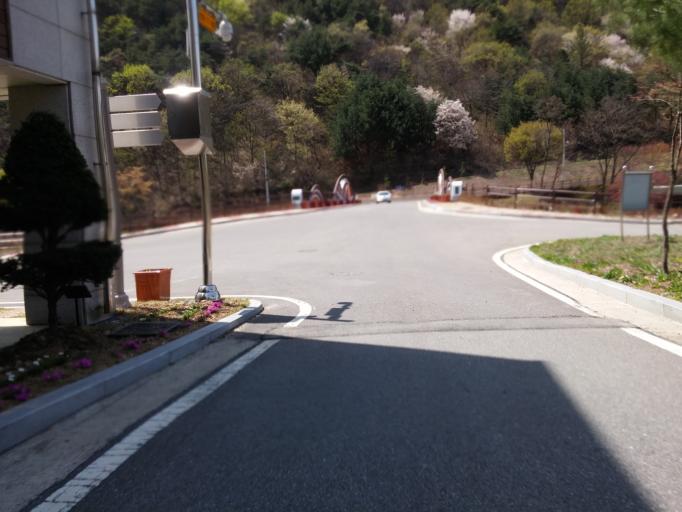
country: KR
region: Chungcheongbuk-do
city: Okcheon
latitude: 36.2453
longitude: 127.5542
